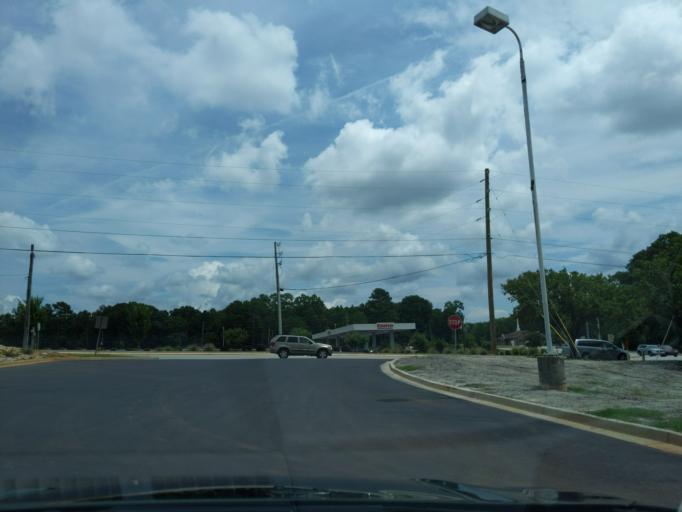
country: US
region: South Carolina
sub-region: Lexington County
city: Seven Oaks
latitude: 34.0688
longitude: -81.1396
